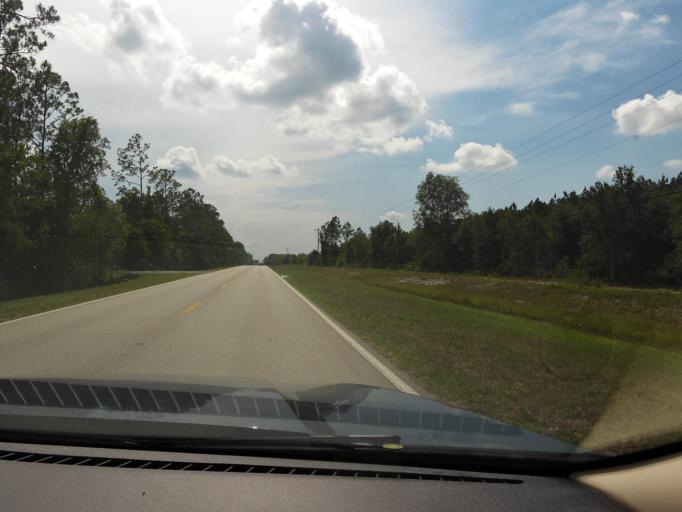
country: US
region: Florida
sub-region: Duval County
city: Baldwin
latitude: 30.2012
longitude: -82.0345
